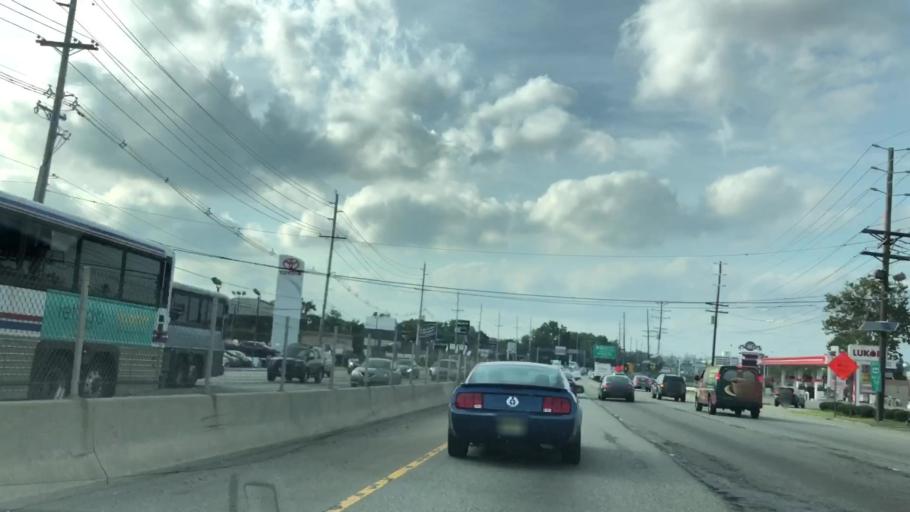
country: US
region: New Jersey
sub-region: Passaic County
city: Little Falls
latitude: 40.8840
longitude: -74.2124
